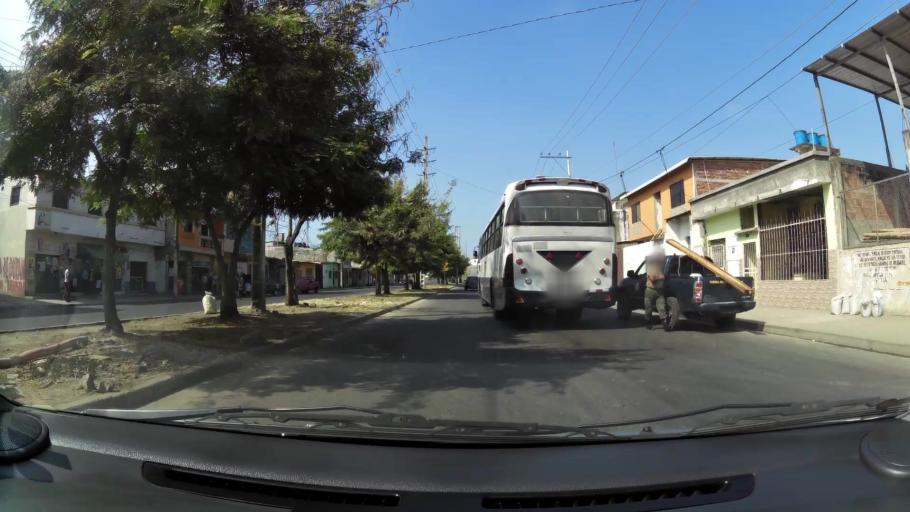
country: EC
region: Guayas
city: Eloy Alfaro
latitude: -2.1694
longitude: -79.8063
